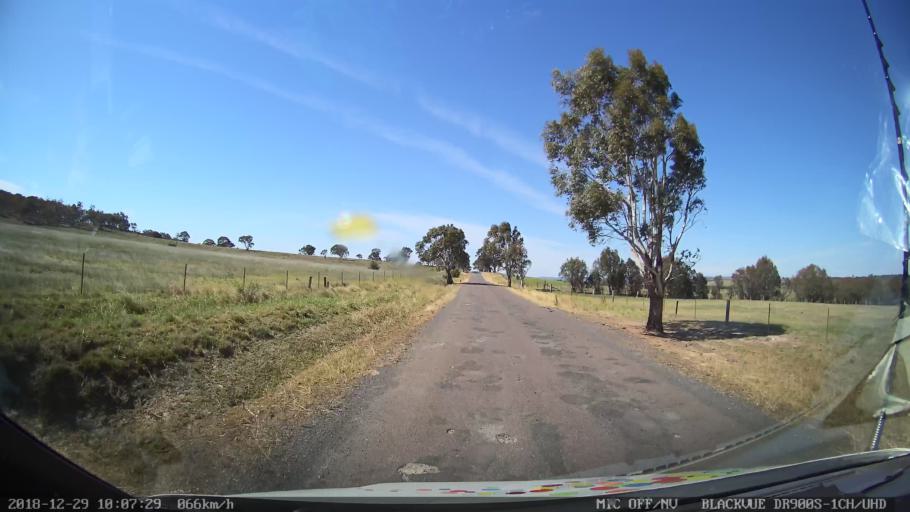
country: AU
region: New South Wales
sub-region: Yass Valley
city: Gundaroo
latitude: -34.8532
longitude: 149.4529
